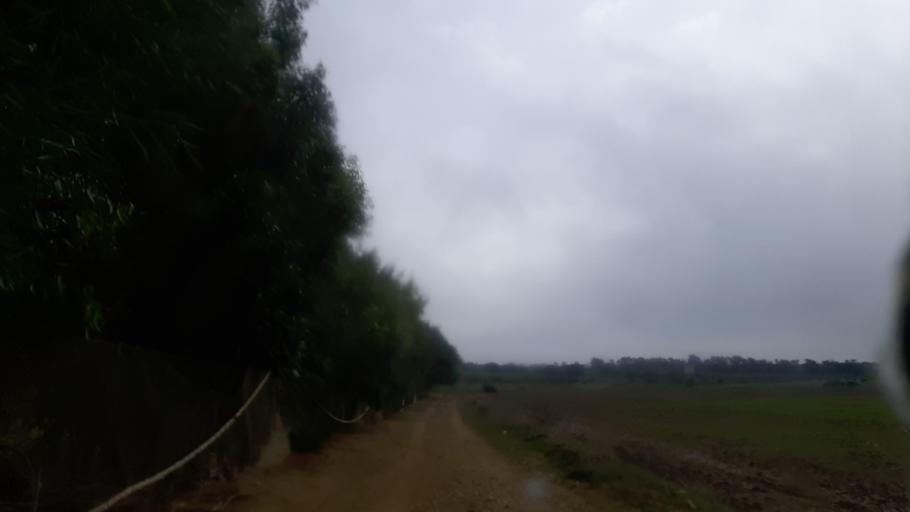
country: TN
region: Nabul
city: Qulaybiyah
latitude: 36.8262
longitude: 11.0361
